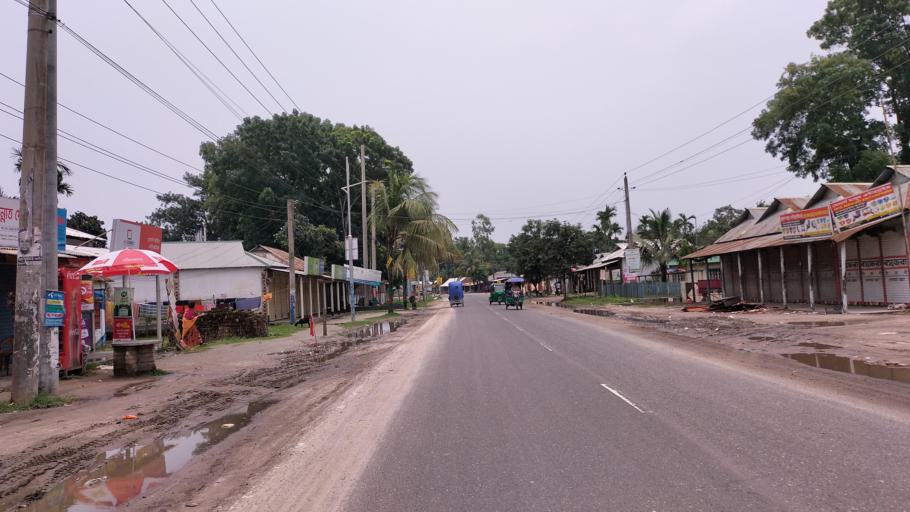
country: BD
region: Dhaka
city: Mymensingh
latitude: 24.7668
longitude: 90.4539
